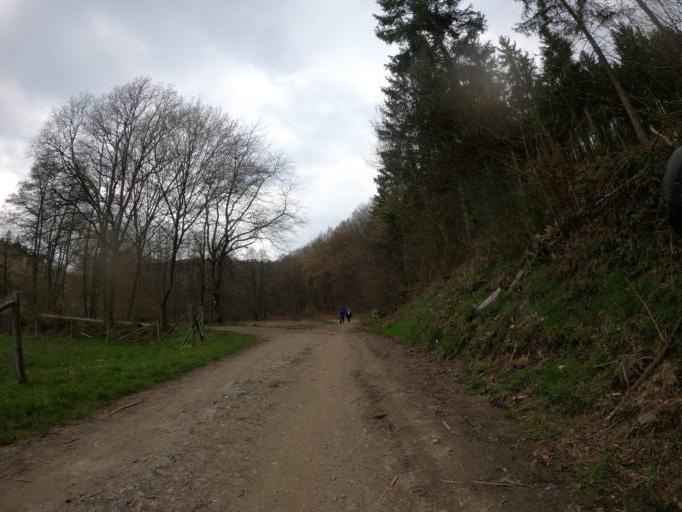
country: DE
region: North Rhine-Westphalia
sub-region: Regierungsbezirk Koln
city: Hurtgenwald
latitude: 50.7005
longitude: 6.3915
